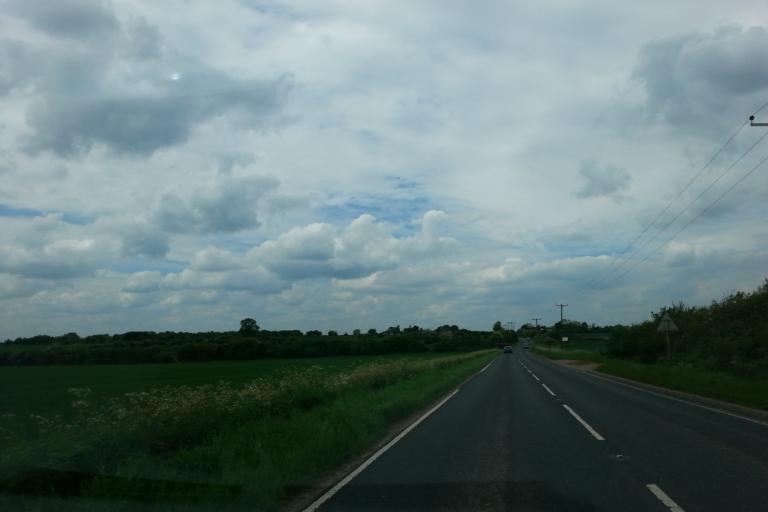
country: GB
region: England
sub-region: Cambridgeshire
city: Warboys
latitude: 52.4101
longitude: -0.1017
